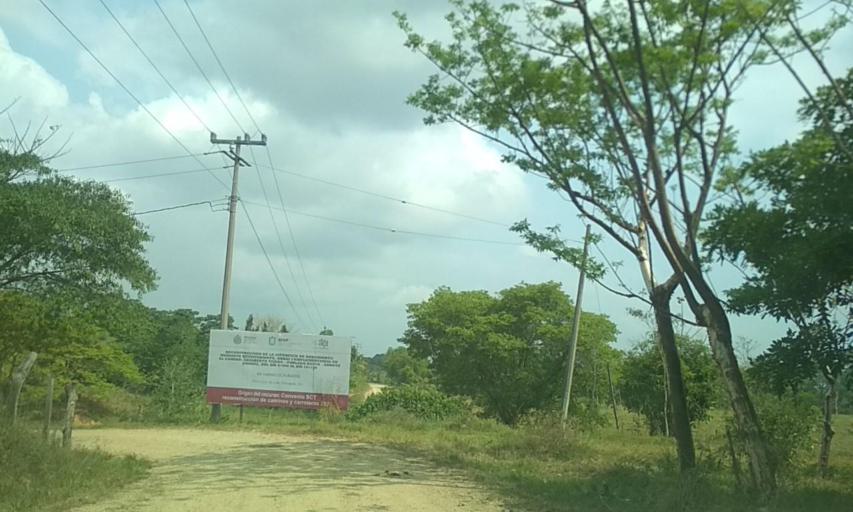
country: MX
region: Tabasco
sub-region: Huimanguillo
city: Francisco Rueda
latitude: 17.6550
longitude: -93.7537
